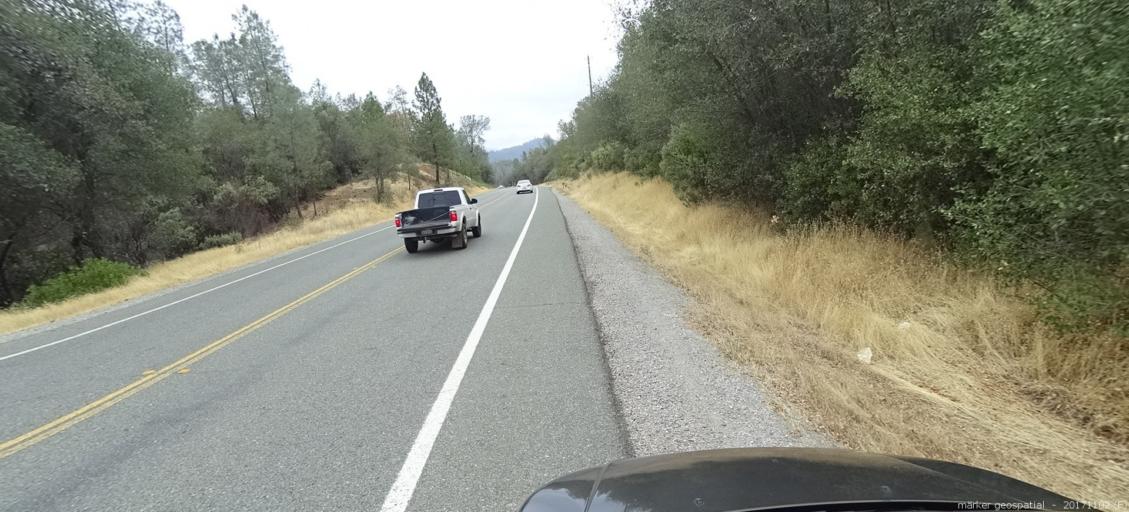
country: US
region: California
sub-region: Shasta County
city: Central Valley (historical)
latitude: 40.6666
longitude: -122.3973
